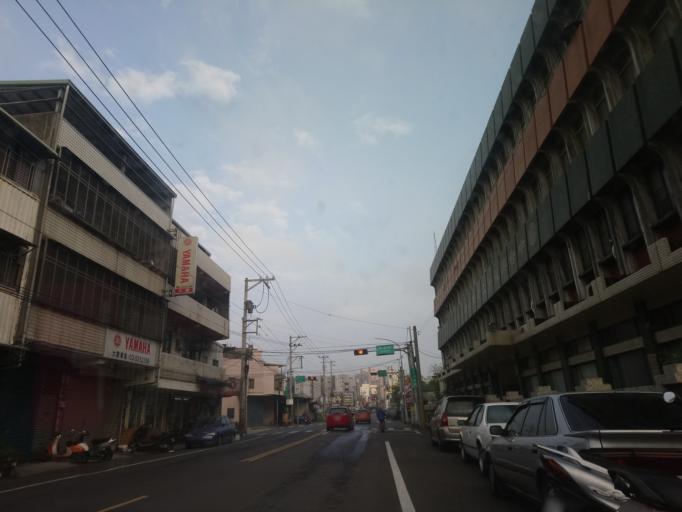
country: TW
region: Taiwan
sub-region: Hsinchu
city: Hsinchu
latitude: 24.7965
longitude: 120.9372
